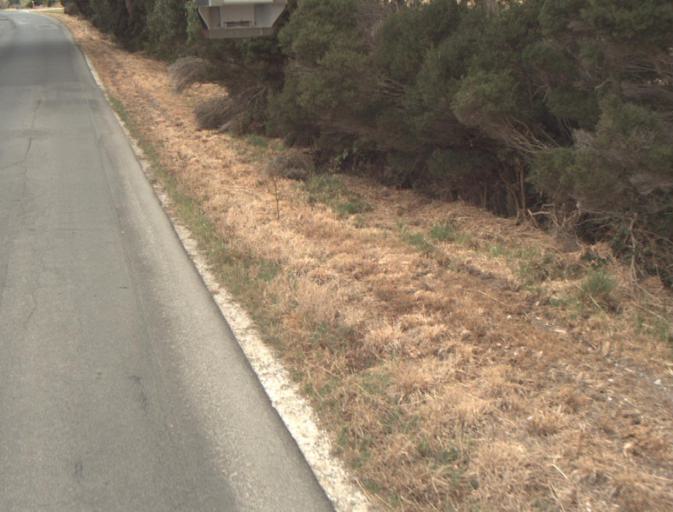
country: AU
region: Tasmania
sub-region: Launceston
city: Mayfield
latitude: -41.2045
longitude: 147.0774
